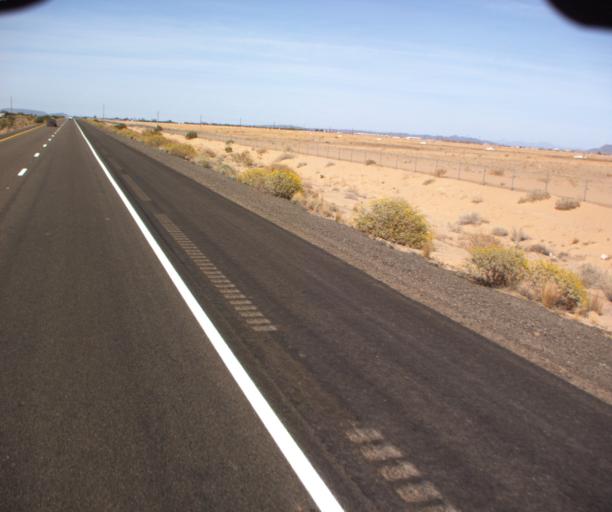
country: US
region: Arizona
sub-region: Yuma County
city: Fortuna Foothills
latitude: 32.6437
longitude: -114.5213
